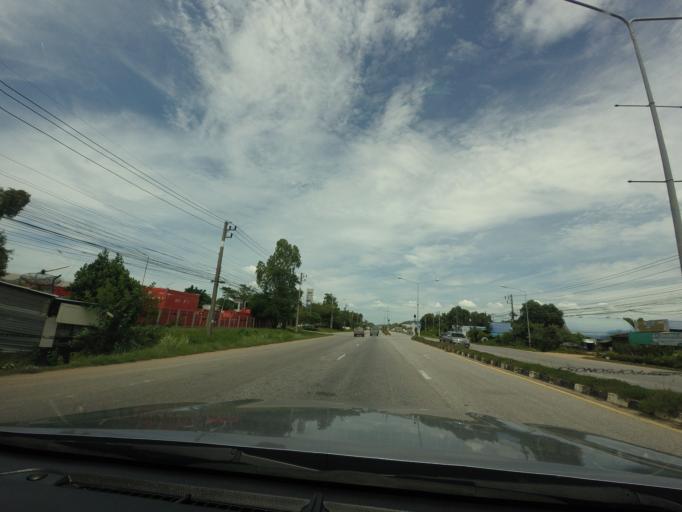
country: TH
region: Songkhla
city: Singhanakhon
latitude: 7.2457
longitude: 100.5406
